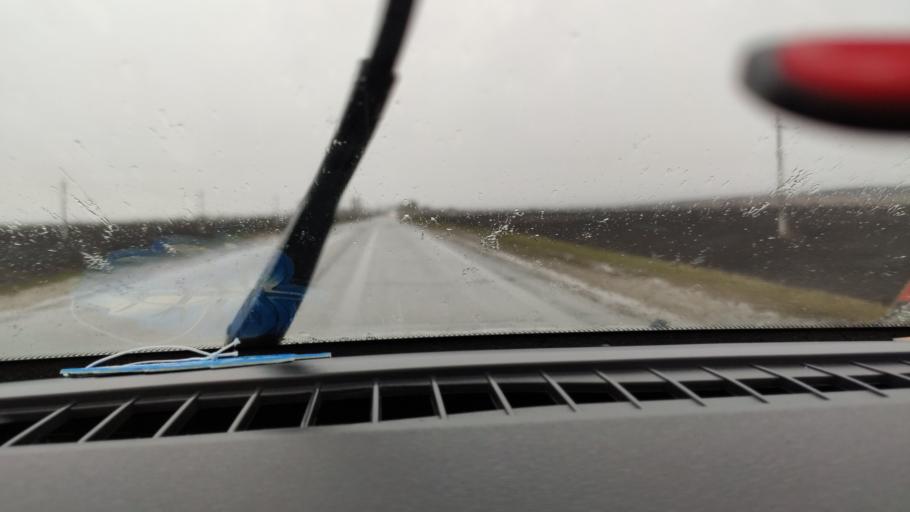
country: RU
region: Samara
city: Chelno-Vershiny
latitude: 54.7005
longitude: 51.1405
